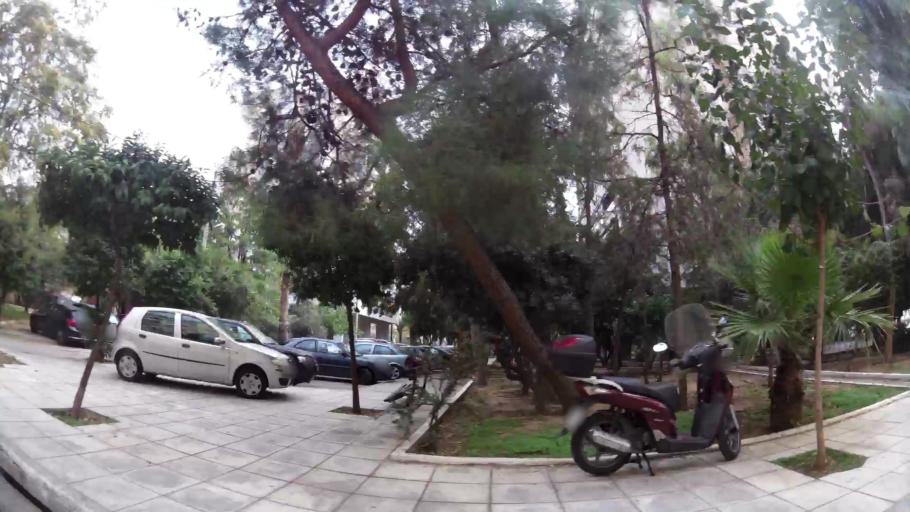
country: GR
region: Attica
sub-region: Nomarchia Athinas
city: Tavros
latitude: 37.9682
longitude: 23.6944
